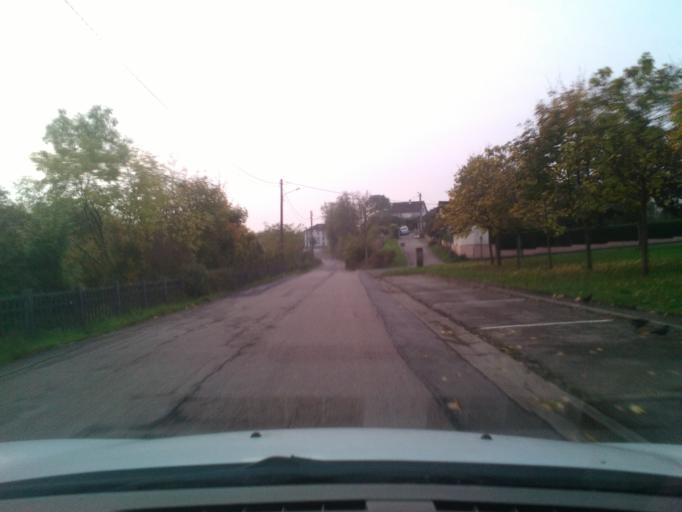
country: FR
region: Lorraine
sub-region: Departement des Vosges
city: Mirecourt
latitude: 48.3013
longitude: 6.1280
